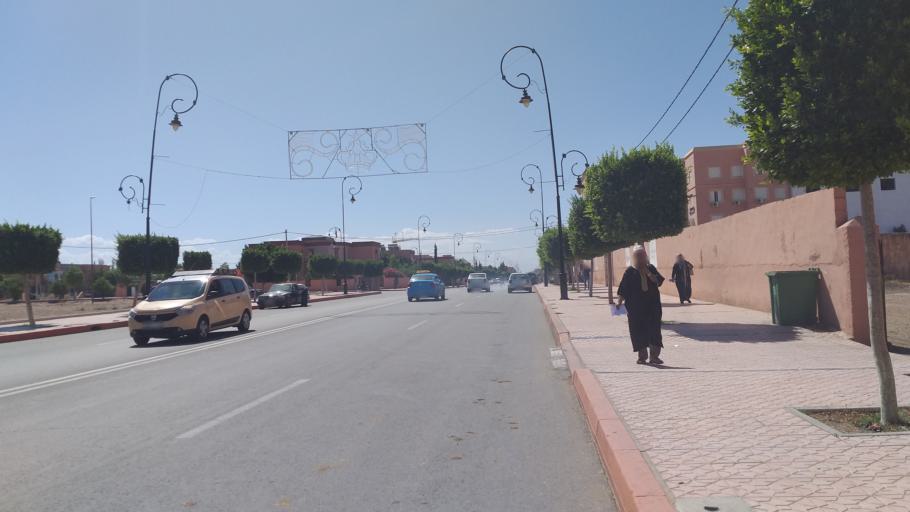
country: MA
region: Marrakech-Tensift-Al Haouz
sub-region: Chichaoua
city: Chichaoua
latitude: 31.5410
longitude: -8.7673
